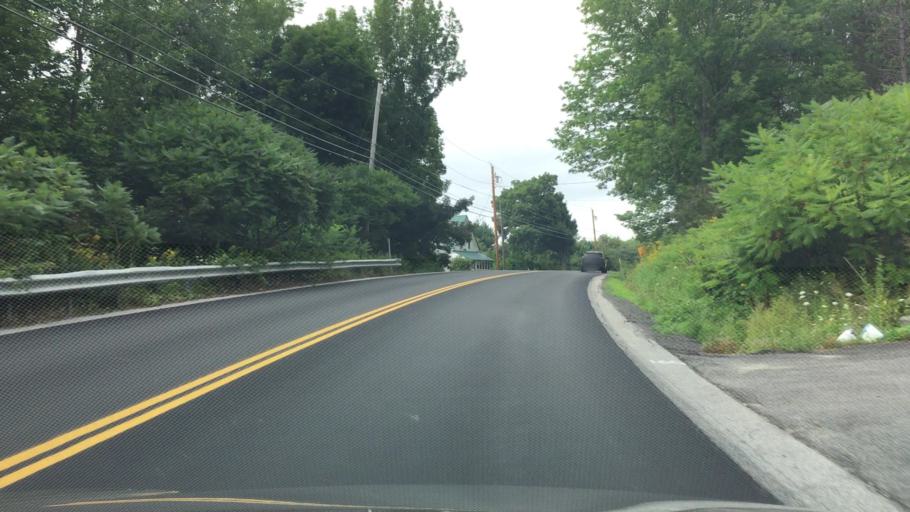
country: US
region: Maine
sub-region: Waldo County
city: Winterport
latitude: 44.6200
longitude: -68.8308
